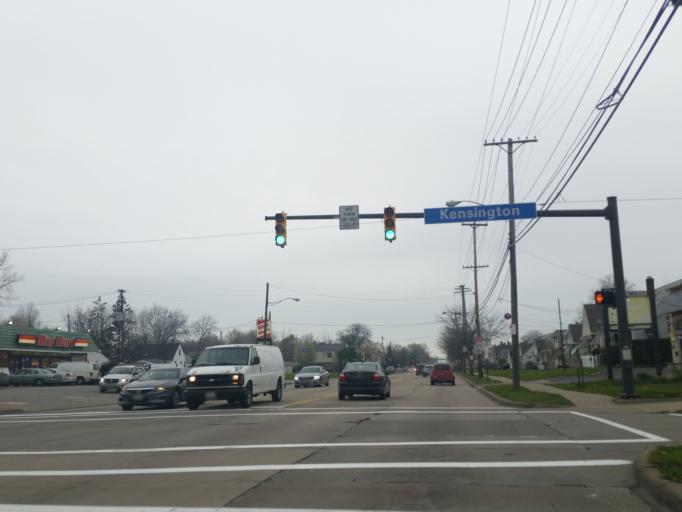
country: US
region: Ohio
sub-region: Cuyahoga County
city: Brooklyn
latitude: 41.4497
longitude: -81.7690
